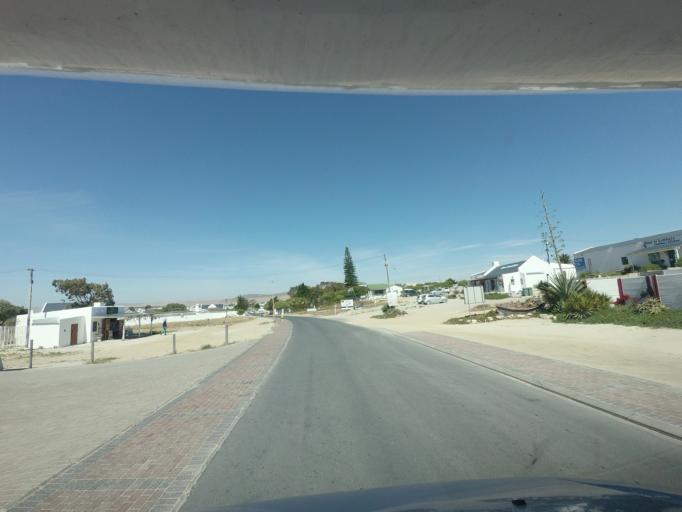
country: ZA
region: Western Cape
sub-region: West Coast District Municipality
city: Vredenburg
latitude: -32.8097
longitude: 17.8921
